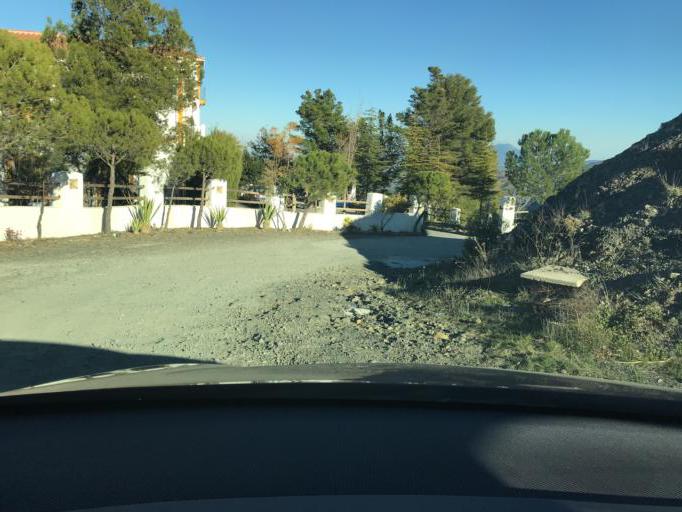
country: ES
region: Andalusia
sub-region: Provincia de Malaga
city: Tolox
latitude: 36.6845
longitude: -4.9178
